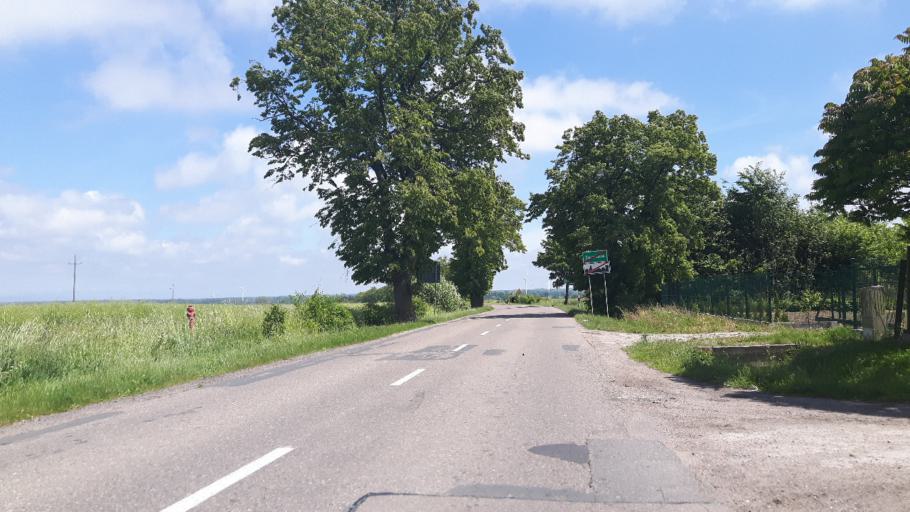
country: PL
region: Pomeranian Voivodeship
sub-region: Powiat slupski
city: Ustka
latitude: 54.5204
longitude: 16.7719
